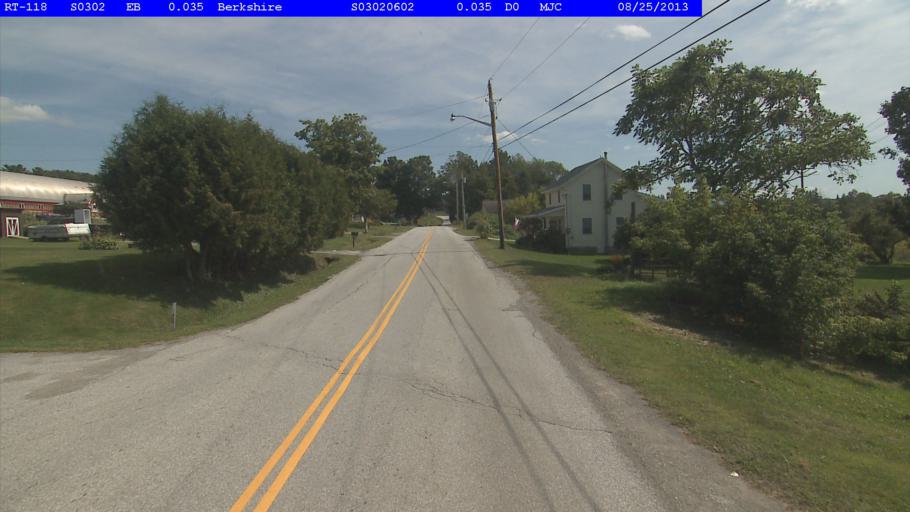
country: US
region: Vermont
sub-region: Franklin County
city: Enosburg Falls
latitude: 44.9891
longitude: -72.8126
